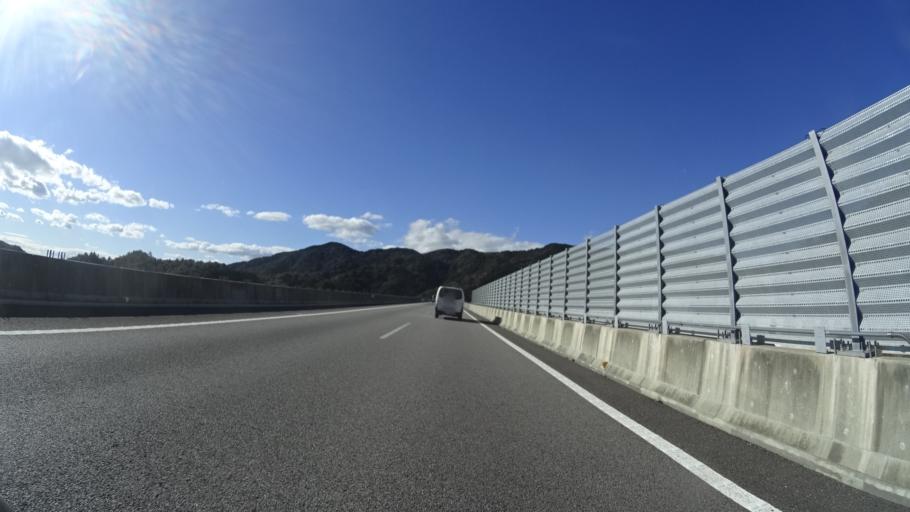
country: JP
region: Aichi
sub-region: Tokai-shi
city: Toyokawa
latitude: 34.8827
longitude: 137.3772
